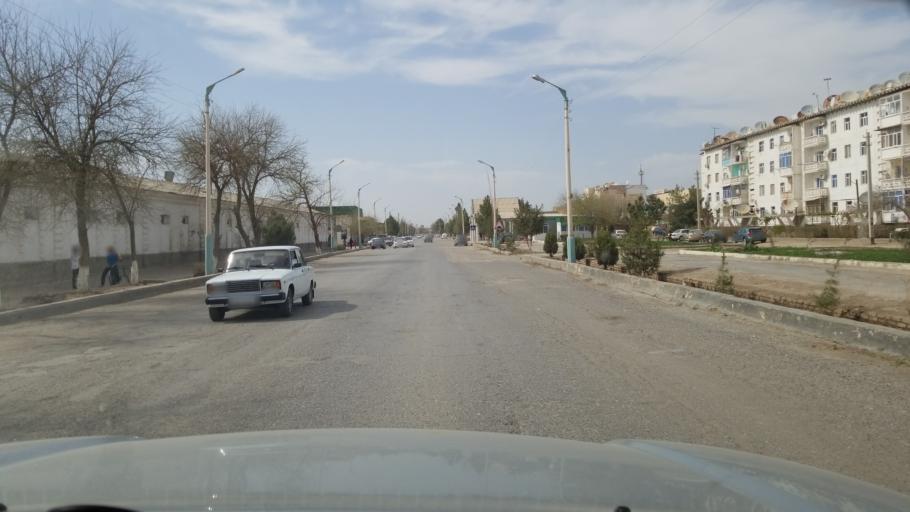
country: TM
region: Lebap
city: Atamyrat
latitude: 37.8414
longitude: 65.2043
